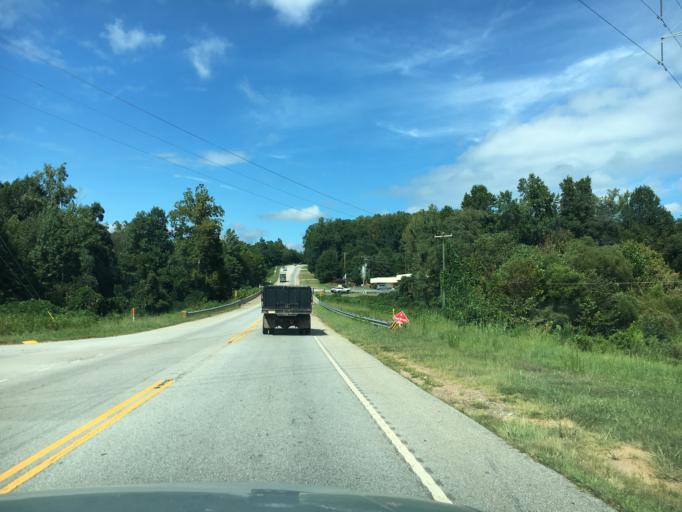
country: US
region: South Carolina
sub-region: Spartanburg County
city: Wellford
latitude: 34.9739
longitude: -82.1188
